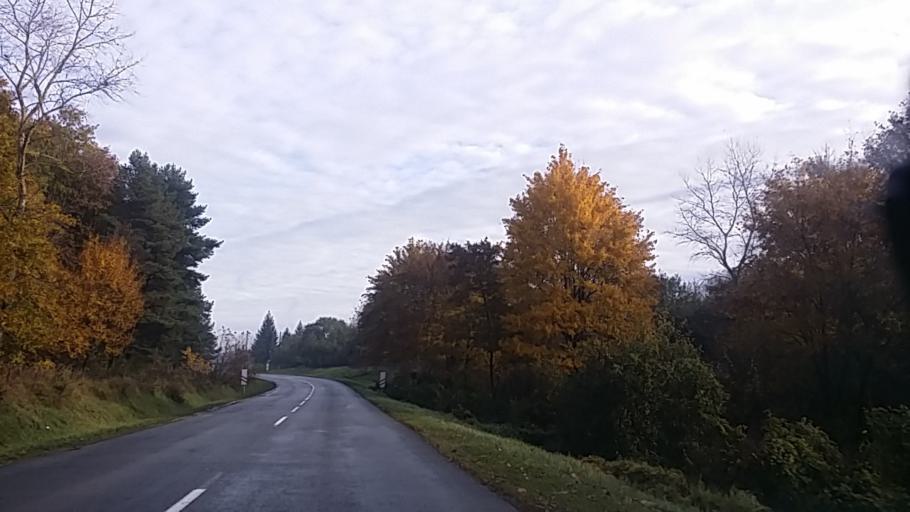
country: HU
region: Heves
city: Szilvasvarad
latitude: 48.0931
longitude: 20.3808
